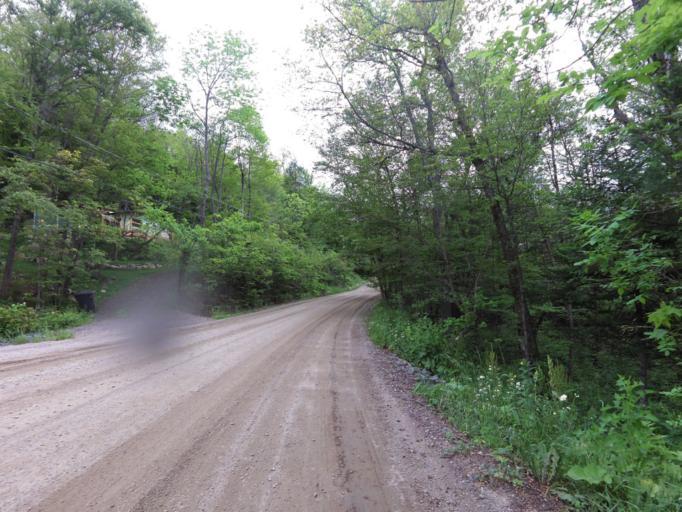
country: CA
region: Quebec
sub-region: Laurentides
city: Mont-Tremblant
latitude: 45.9303
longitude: -74.6590
